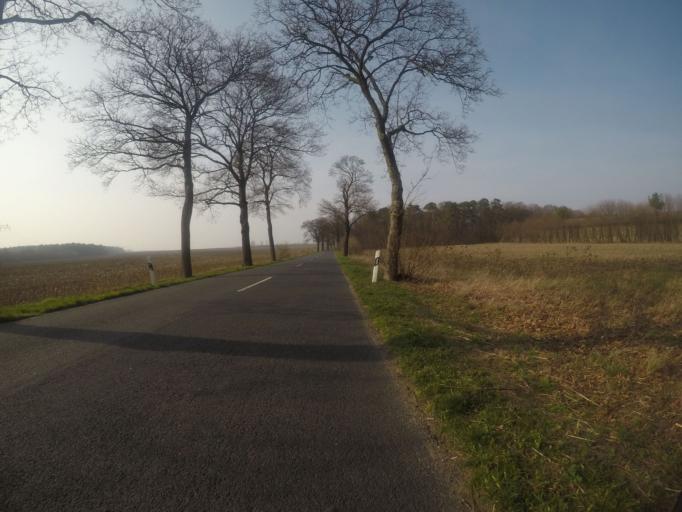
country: DE
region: Brandenburg
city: Schonefeld
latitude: 52.3391
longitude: 13.4918
